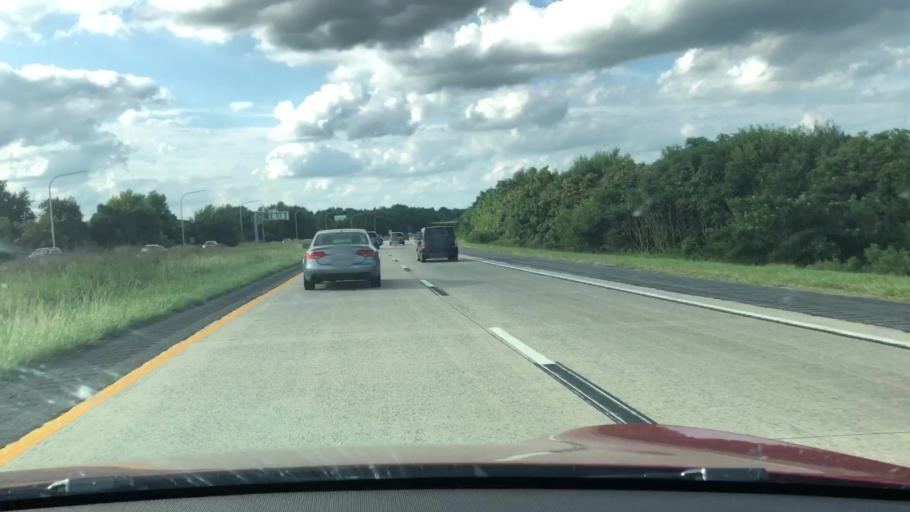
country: US
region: Delaware
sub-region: Kent County
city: Smyrna
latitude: 39.2853
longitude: -75.5907
